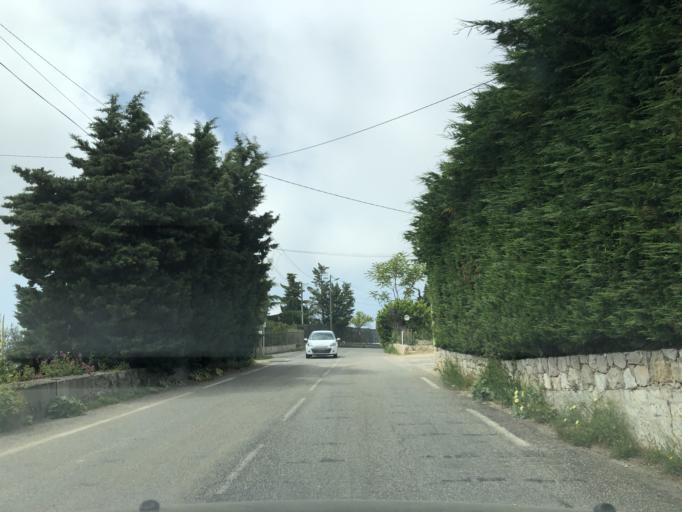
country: FR
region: Provence-Alpes-Cote d'Azur
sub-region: Departement des Alpes-Maritimes
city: Beaulieu-sur-Mer
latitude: 43.7238
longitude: 7.3365
